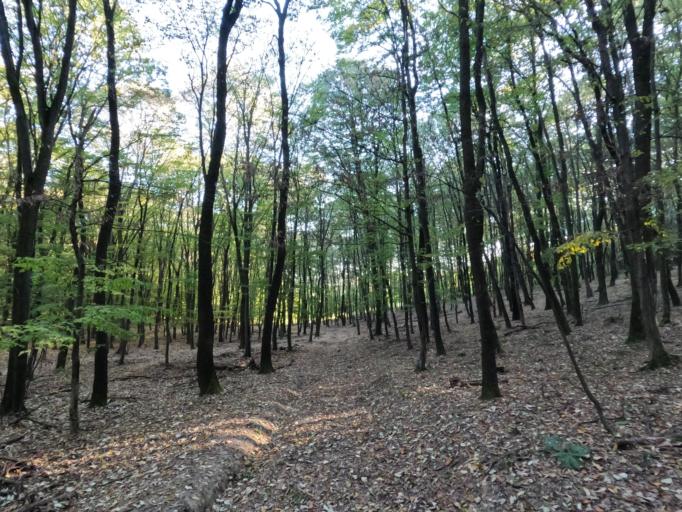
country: HU
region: Tolna
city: Szekszard
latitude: 46.3092
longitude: 18.6532
